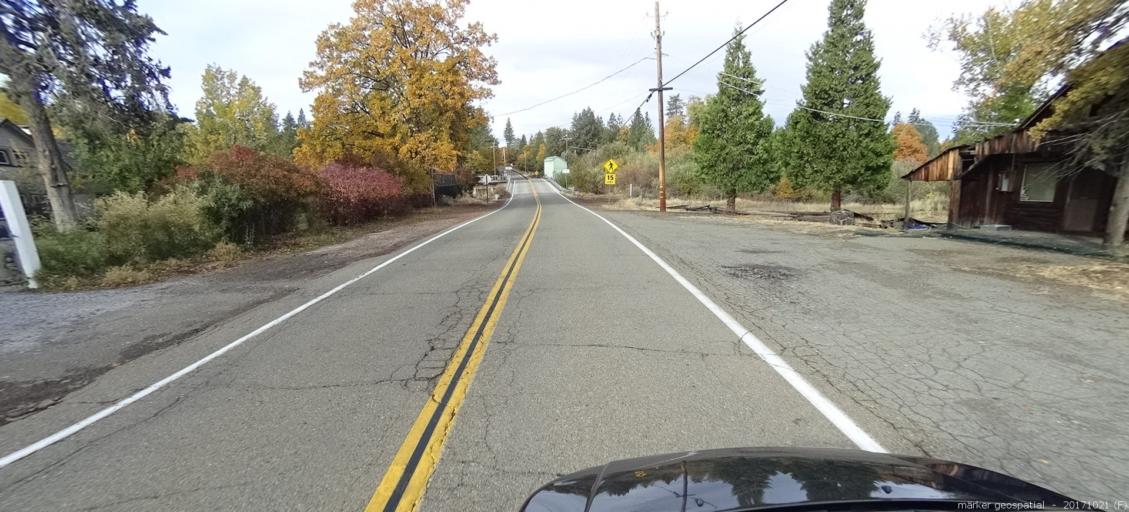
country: US
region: California
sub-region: Shasta County
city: Burney
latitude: 40.9191
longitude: -121.5507
